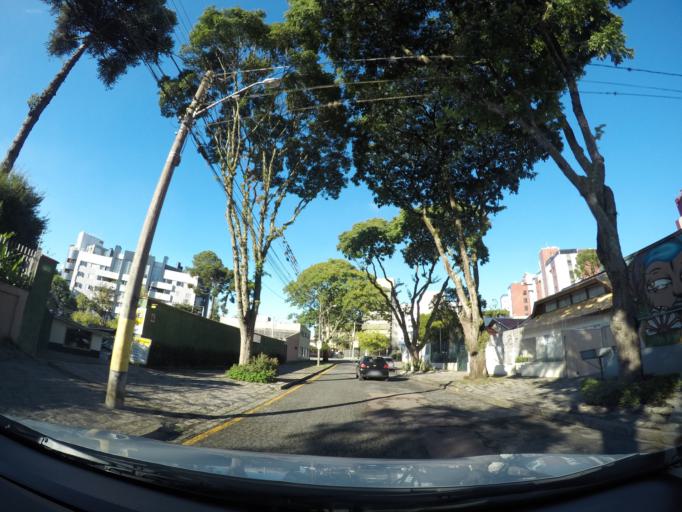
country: BR
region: Parana
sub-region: Curitiba
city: Curitiba
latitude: -25.4182
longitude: -49.2610
